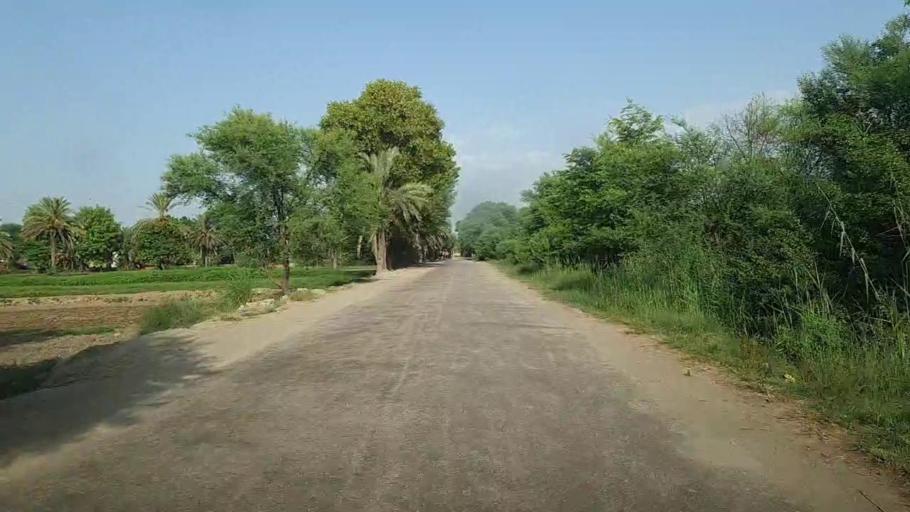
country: PK
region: Sindh
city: Khairpur
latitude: 28.0746
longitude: 69.8205
